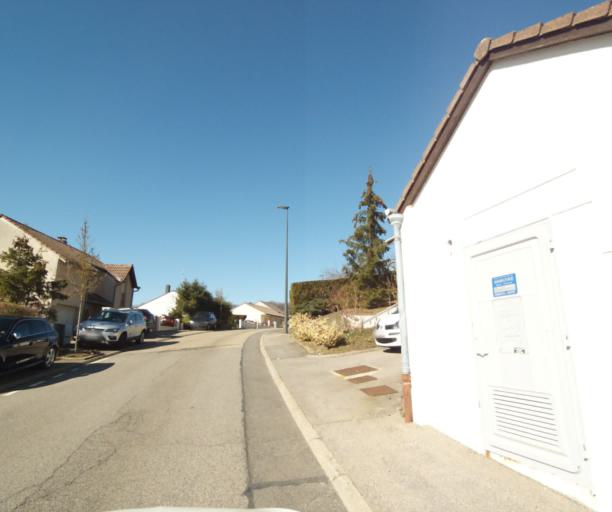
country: FR
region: Lorraine
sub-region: Departement de Meurthe-et-Moselle
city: Essey-les-Nancy
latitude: 48.7125
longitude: 6.2223
